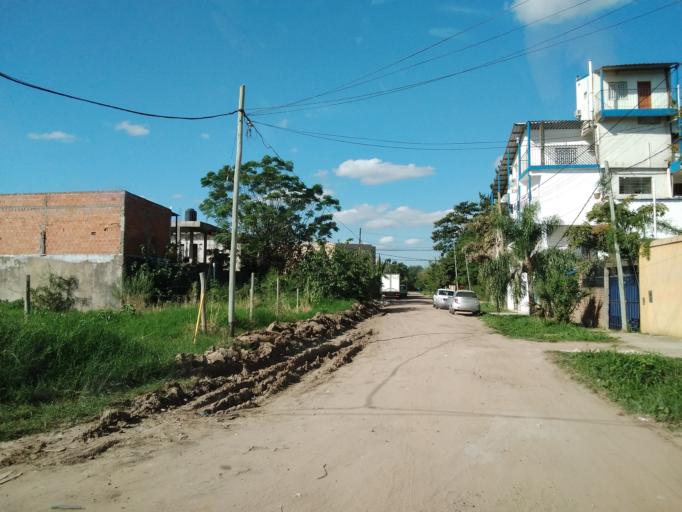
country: AR
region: Corrientes
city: Corrientes
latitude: -27.4631
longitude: -58.7791
